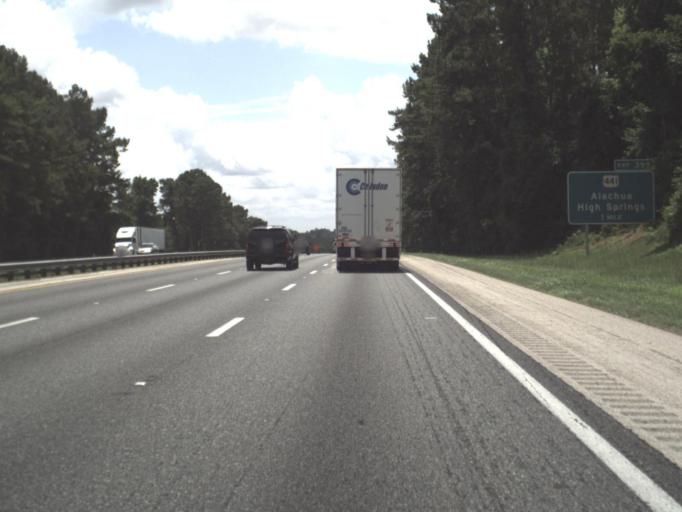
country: US
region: Florida
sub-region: Alachua County
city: High Springs
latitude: 29.8195
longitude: -82.5173
